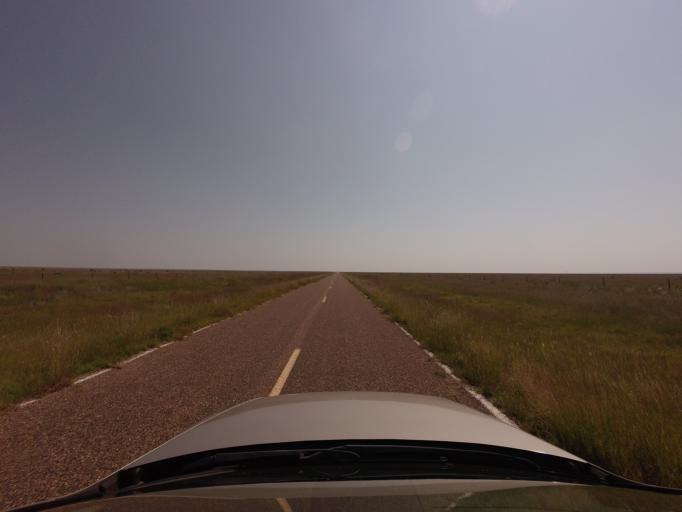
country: US
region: New Mexico
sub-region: Curry County
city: Cannon Air Force Base
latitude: 34.6332
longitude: -103.4411
